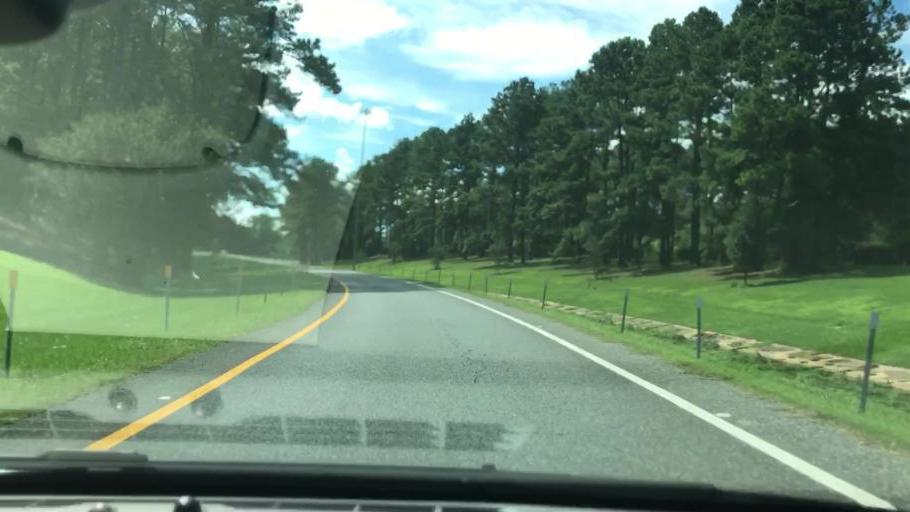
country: US
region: Florida
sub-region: Leon County
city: Tallahassee
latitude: 30.4854
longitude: -84.1598
